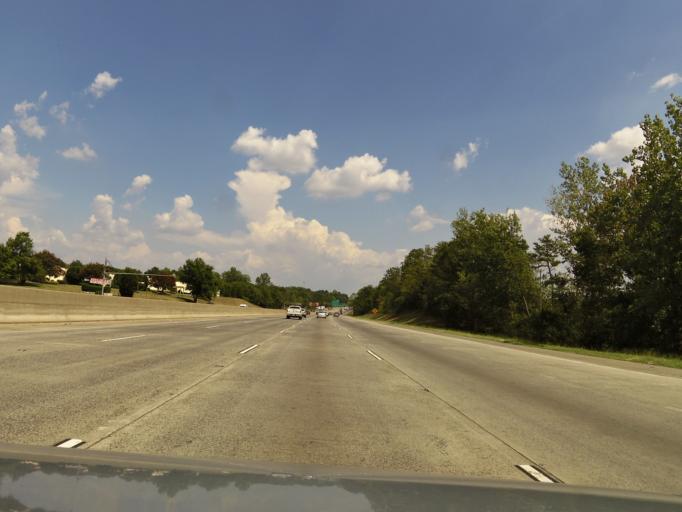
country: US
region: North Carolina
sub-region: Gaston County
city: Belmont
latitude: 35.2576
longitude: -80.9971
